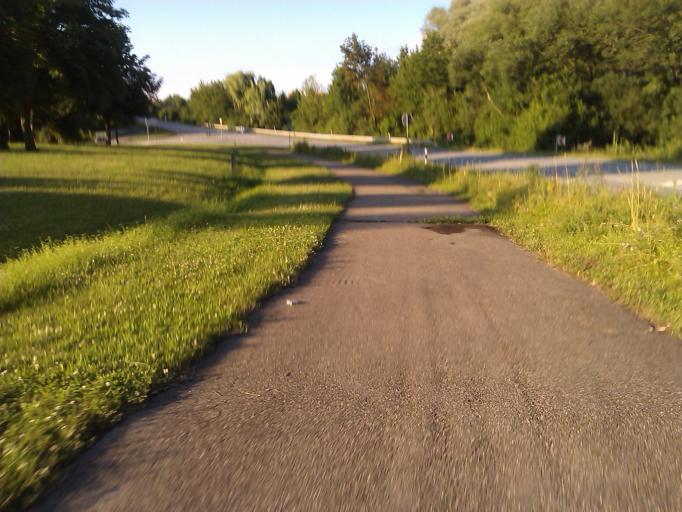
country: DE
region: Baden-Wuerttemberg
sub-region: Regierungsbezirk Stuttgart
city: Neckarwestheim
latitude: 49.0390
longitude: 9.1797
